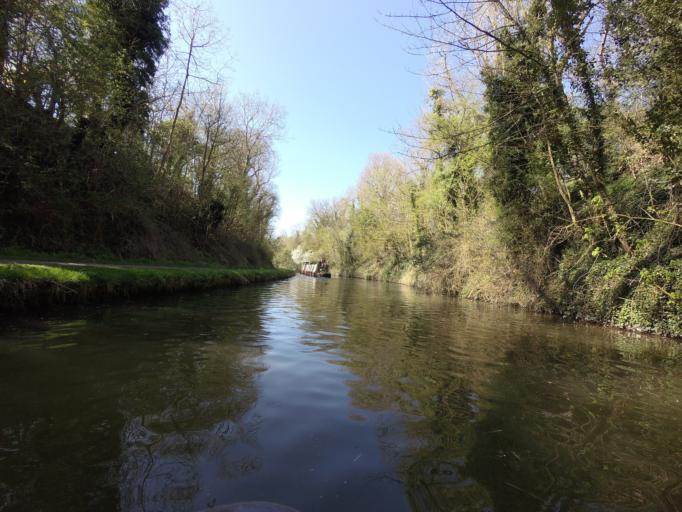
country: GB
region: England
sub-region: Hertfordshire
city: Tring
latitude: 51.8105
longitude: -0.6423
